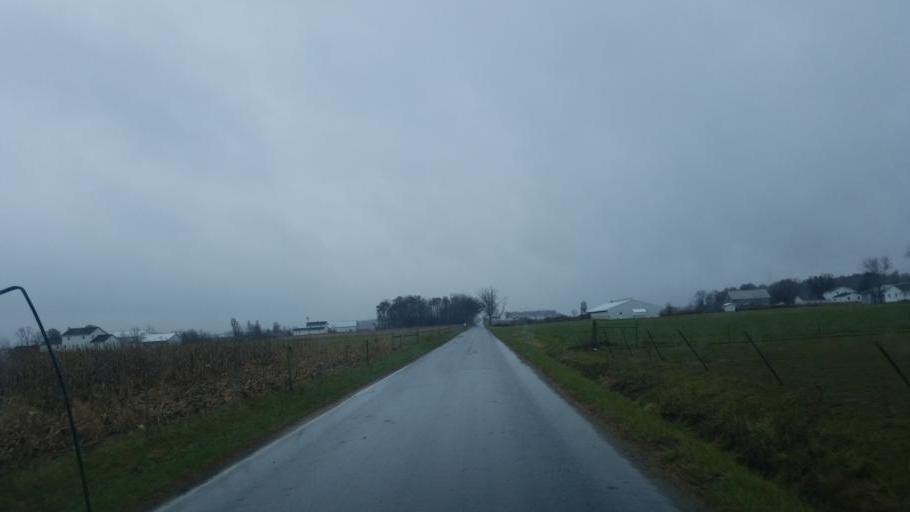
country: US
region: Indiana
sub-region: Adams County
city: Berne
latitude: 40.6285
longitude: -84.8784
